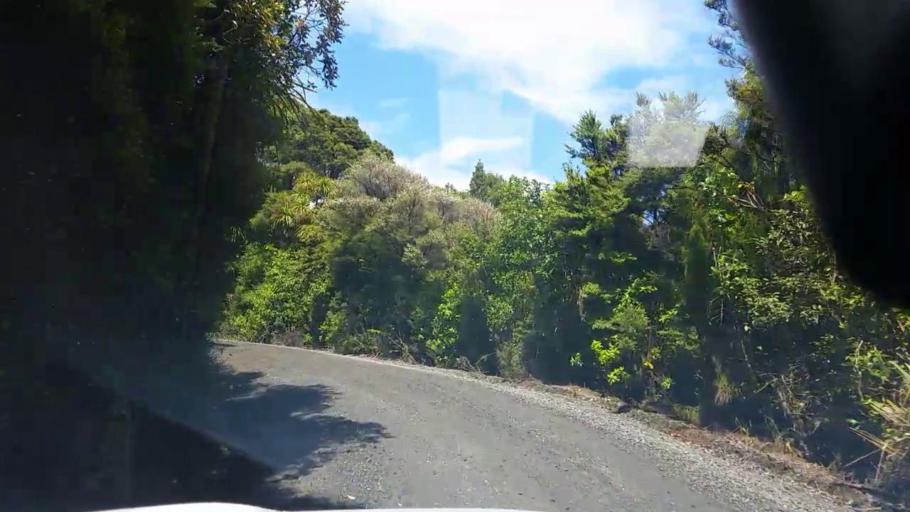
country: NZ
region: Auckland
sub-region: Auckland
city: Titirangi
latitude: -36.9365
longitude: 174.5184
